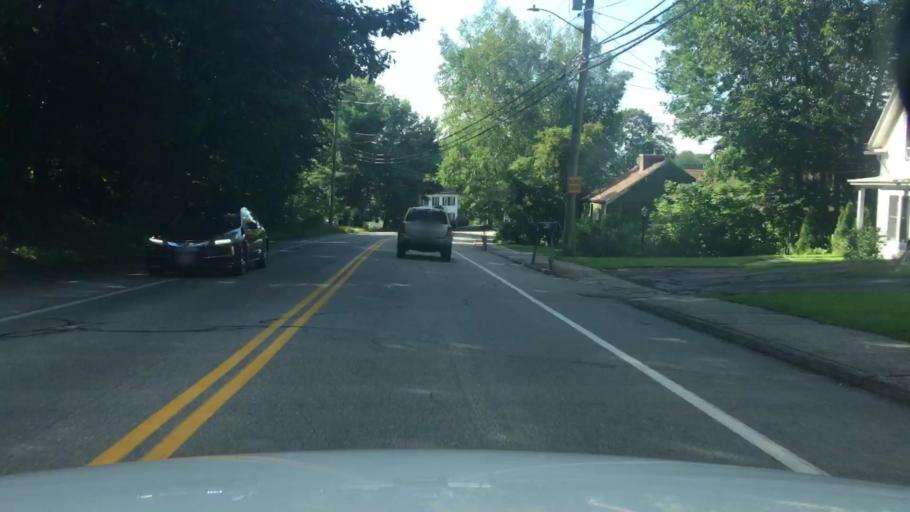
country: US
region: New Hampshire
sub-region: Strafford County
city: Dover
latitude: 43.1749
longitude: -70.8754
